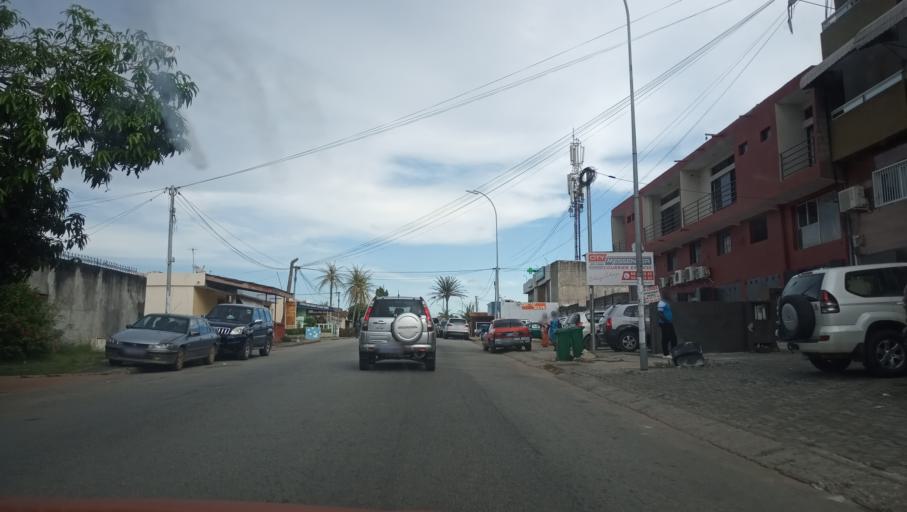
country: CI
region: Lagunes
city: Abidjan
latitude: 5.3495
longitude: -3.9812
